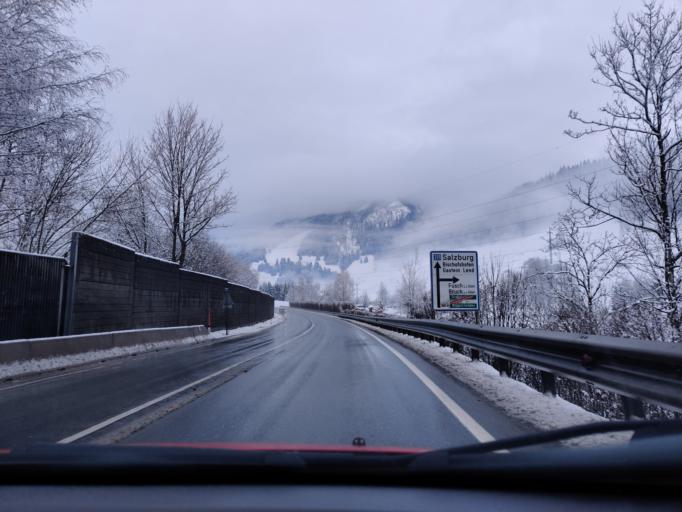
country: AT
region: Salzburg
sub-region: Politischer Bezirk Zell am See
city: Bruck an der Grossglocknerstrasse
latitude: 47.2824
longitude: 12.8126
